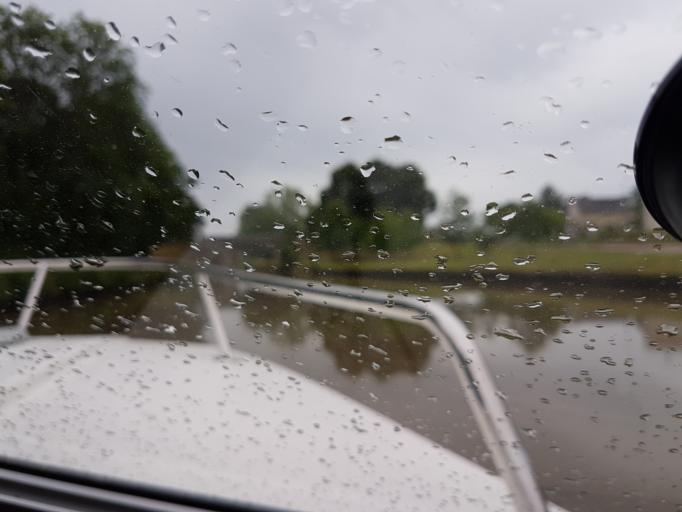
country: FR
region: Bourgogne
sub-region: Departement de la Nievre
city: Corbigny
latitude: 47.3633
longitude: 3.6178
